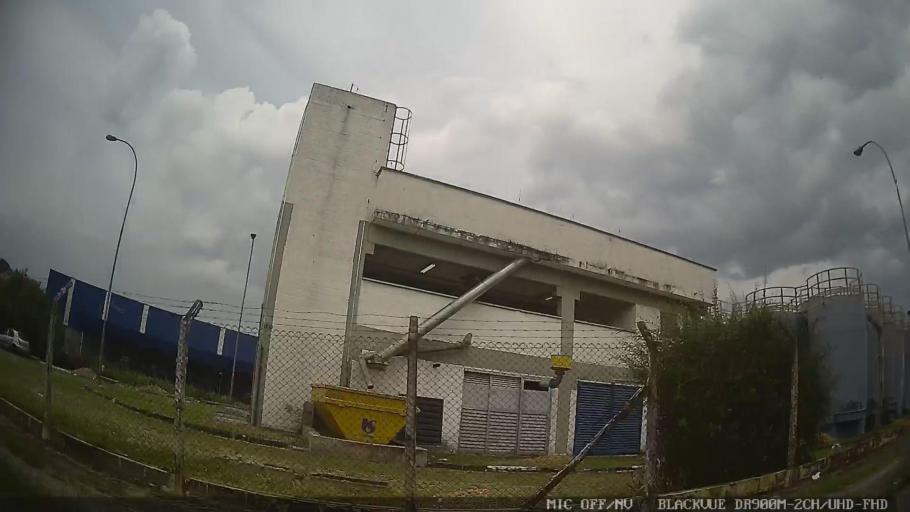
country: BR
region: Sao Paulo
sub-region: Aruja
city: Aruja
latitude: -23.4427
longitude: -46.3160
